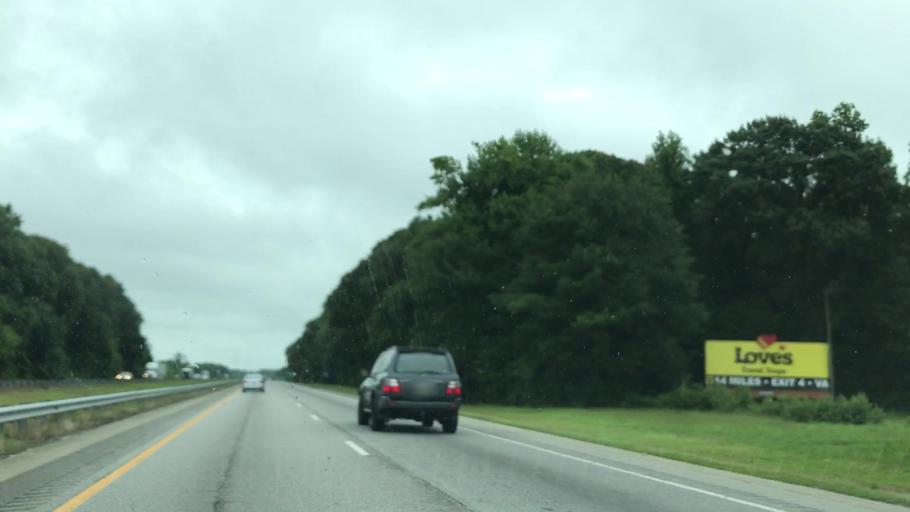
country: US
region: North Carolina
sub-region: Halifax County
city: Weldon
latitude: 36.4605
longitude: -77.6143
